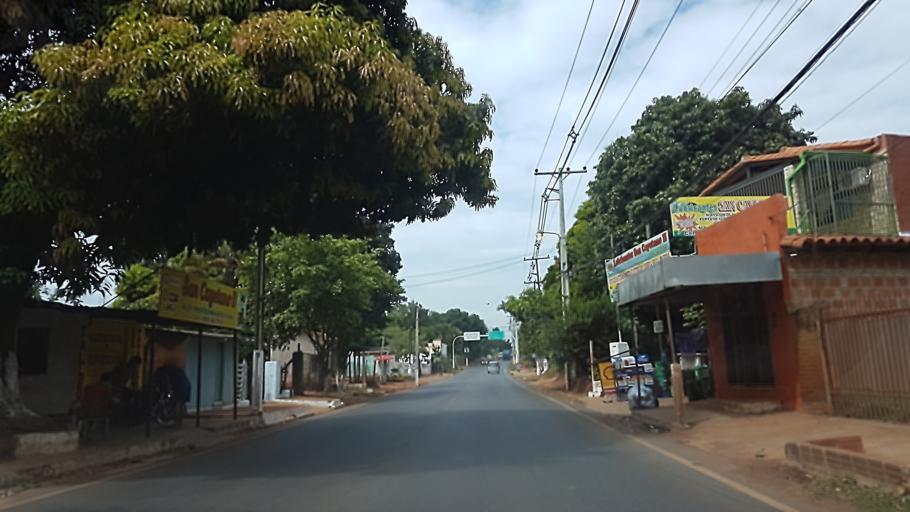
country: PY
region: Central
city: Capiata
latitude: -25.3677
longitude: -57.4501
